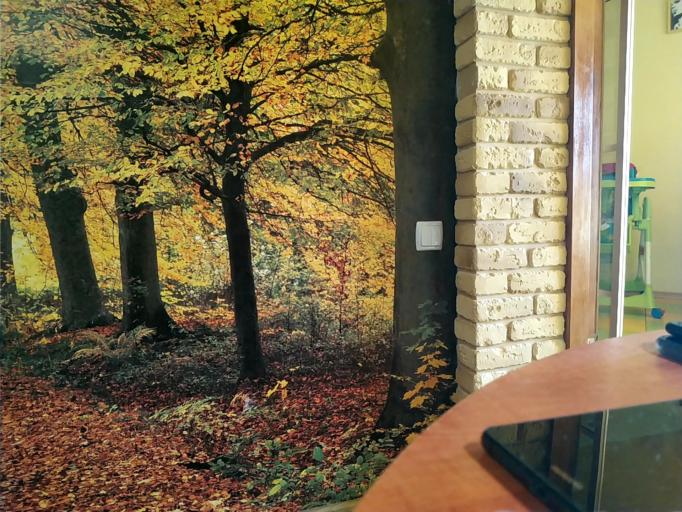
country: RU
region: Kaluga
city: Medyn'
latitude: 54.9578
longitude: 35.8746
